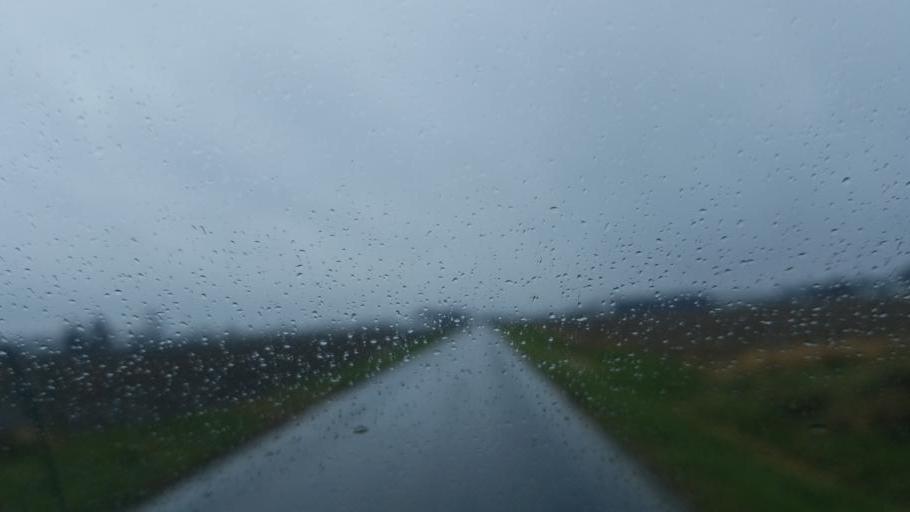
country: US
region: Indiana
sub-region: Adams County
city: Berne
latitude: 40.6336
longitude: -84.8783
